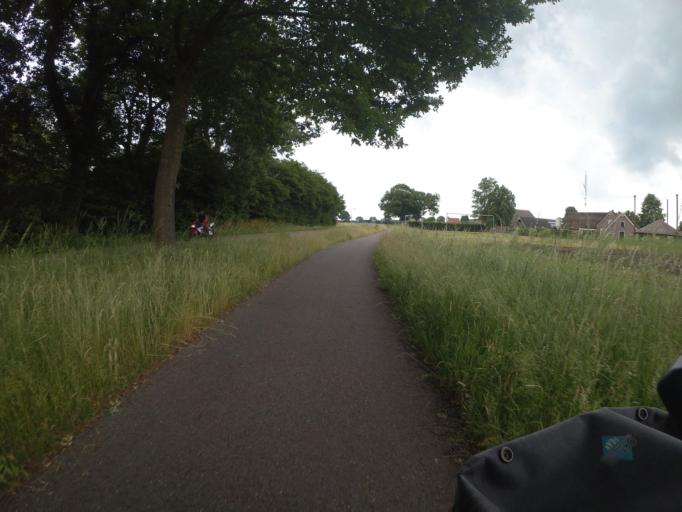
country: NL
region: Overijssel
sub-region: Gemeente Twenterand
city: Vroomshoop
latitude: 52.5234
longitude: 6.5605
